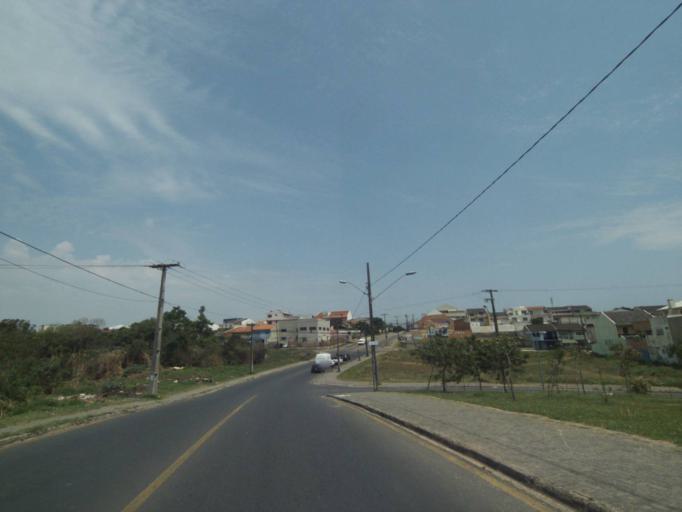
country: BR
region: Parana
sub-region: Curitiba
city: Curitiba
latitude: -25.4816
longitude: -49.3361
